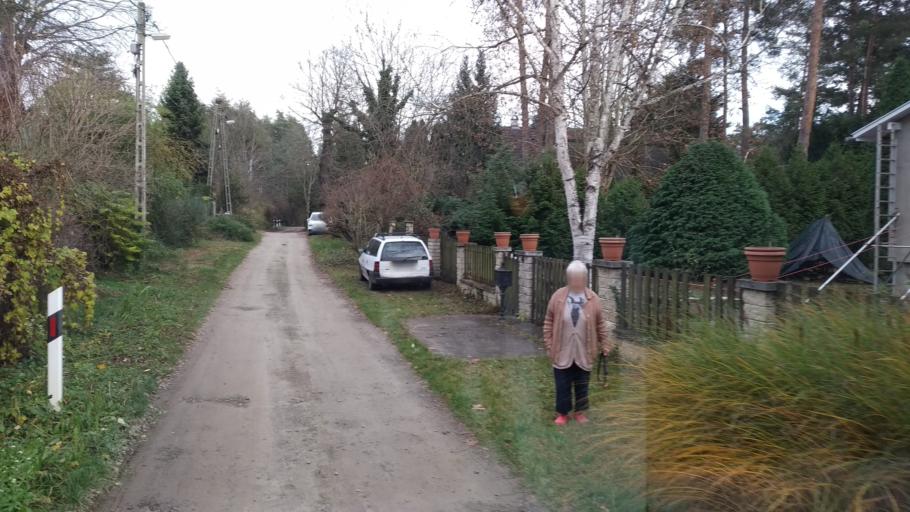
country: HU
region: Pest
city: Szentendre
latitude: 47.6664
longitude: 19.1054
